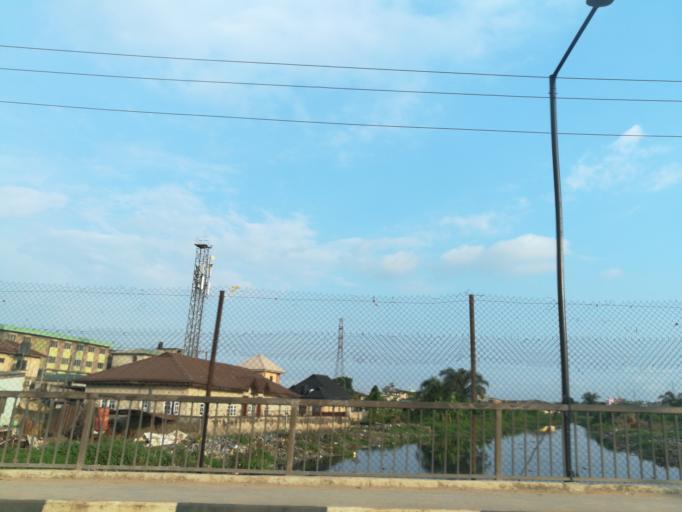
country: NG
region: Lagos
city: Ojota
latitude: 6.5858
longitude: 3.3930
